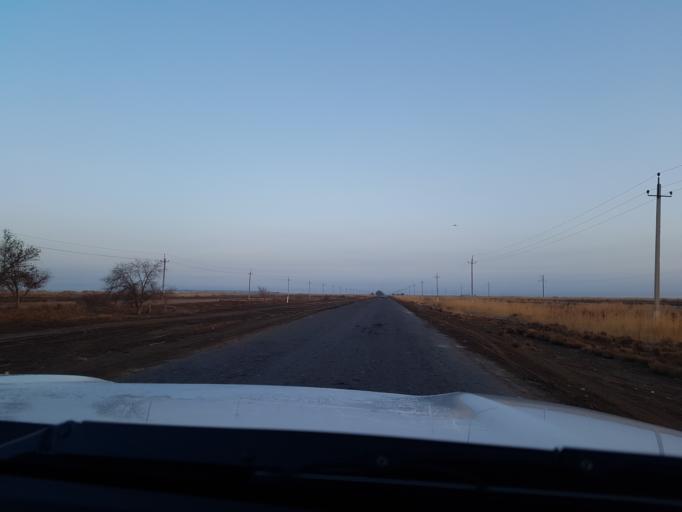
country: TM
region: Dasoguz
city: Koeneuergench
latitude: 41.7501
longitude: 58.6894
